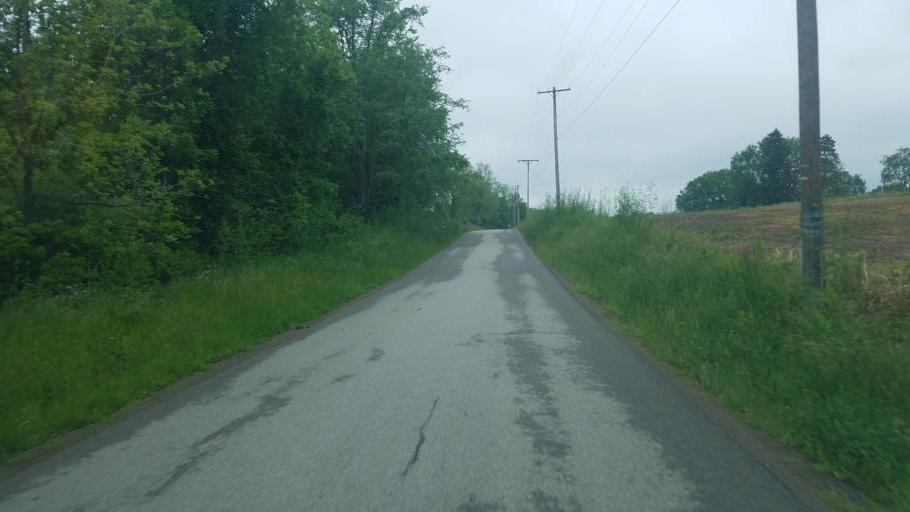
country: US
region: Ohio
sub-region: Richland County
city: Lincoln Heights
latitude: 40.7227
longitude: -82.4425
